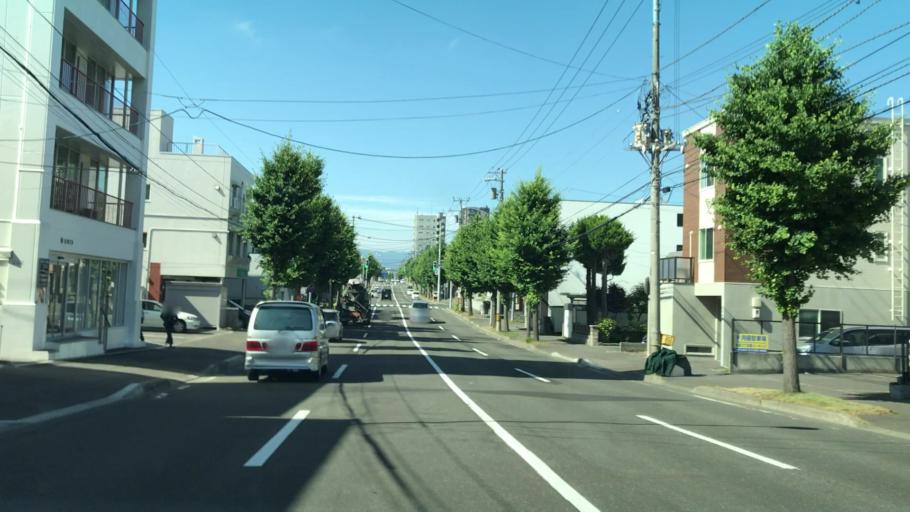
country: JP
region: Hokkaido
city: Sapporo
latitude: 43.0487
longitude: 141.4088
